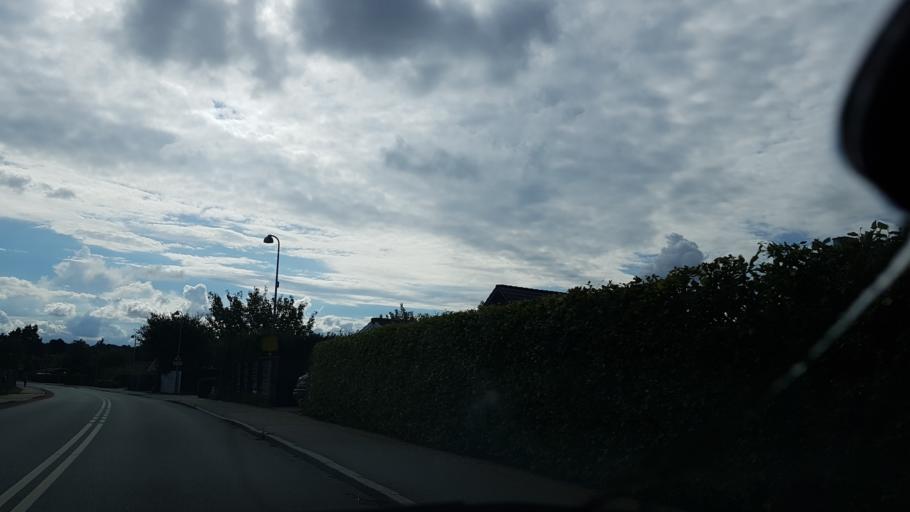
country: DK
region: Capital Region
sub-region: Helsingor Kommune
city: Espergaerde
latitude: 55.9903
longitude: 12.5419
